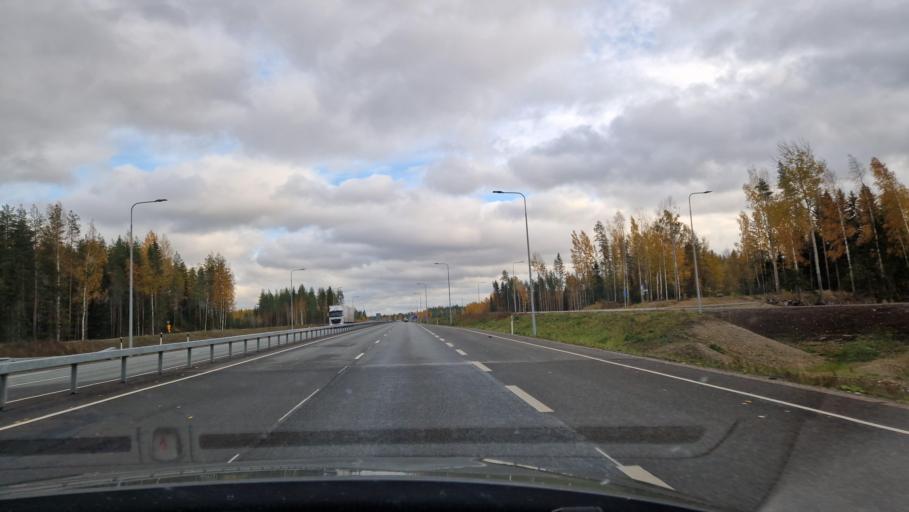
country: FI
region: Southern Savonia
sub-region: Pieksaemaeki
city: Juva
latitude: 61.8803
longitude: 27.7742
